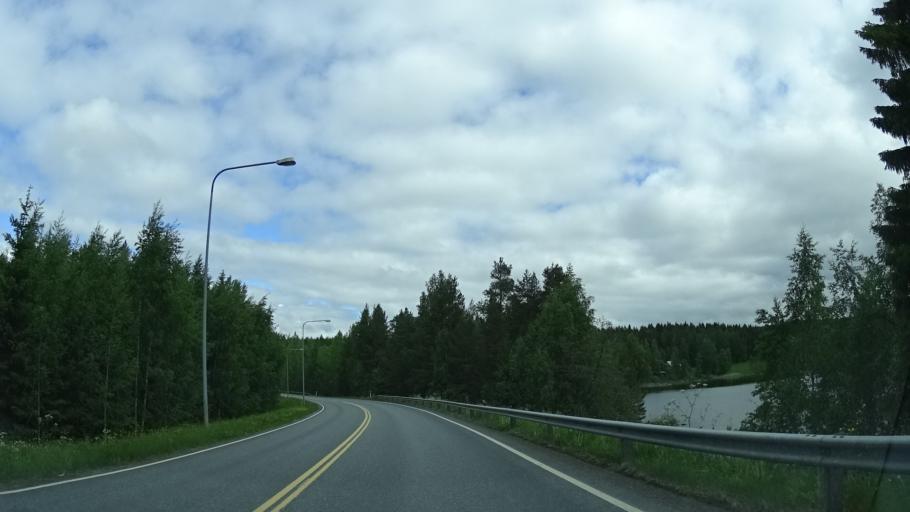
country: FI
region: Central Finland
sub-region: Jyvaeskylae
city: Korpilahti
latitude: 62.0024
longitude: 25.6799
